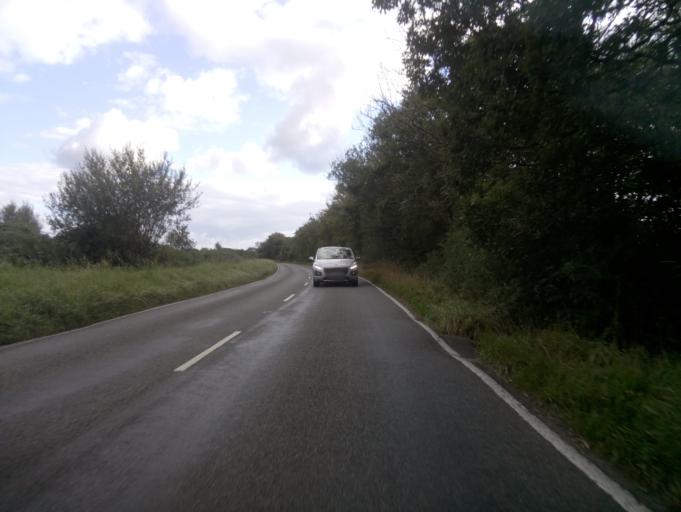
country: GB
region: England
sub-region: Devon
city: Honiton
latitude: 50.7660
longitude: -3.2131
